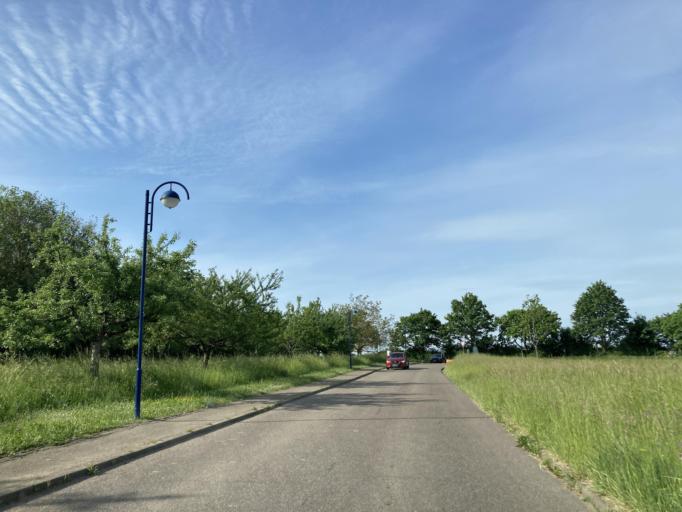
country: DE
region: Baden-Wuerttemberg
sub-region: Karlsruhe Region
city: Malsch
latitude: 49.2148
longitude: 8.6715
